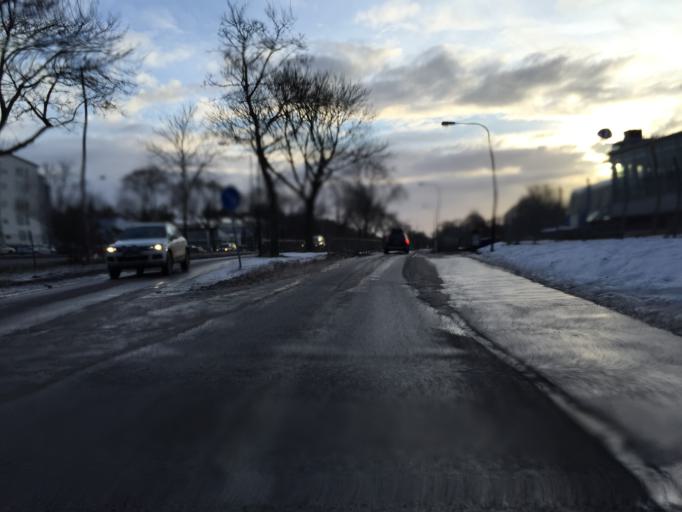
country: SE
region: Stockholm
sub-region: Stockholms Kommun
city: Bromma
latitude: 59.3423
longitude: 17.9247
